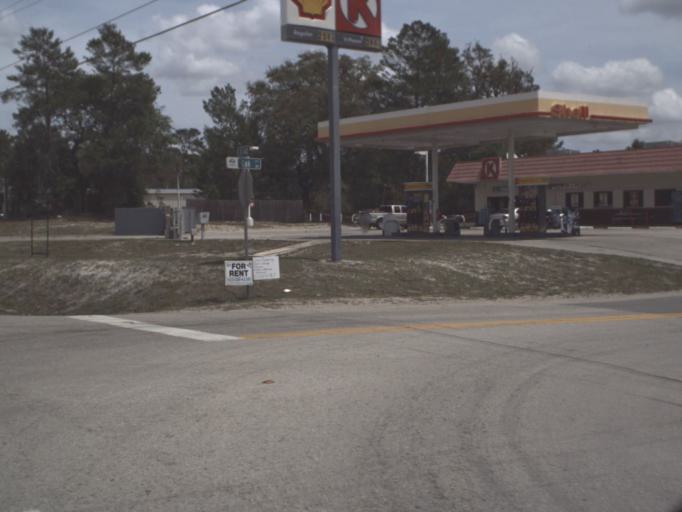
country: US
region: Florida
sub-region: Lake County
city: Lake Mack-Forest Hills
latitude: 28.9412
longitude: -81.4302
